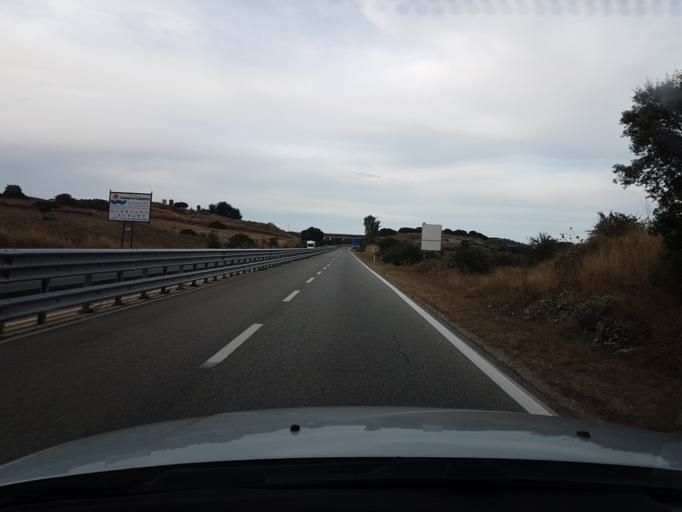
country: IT
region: Sardinia
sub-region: Provincia di Nuoro
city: Oniferi
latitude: 40.2896
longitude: 9.1675
